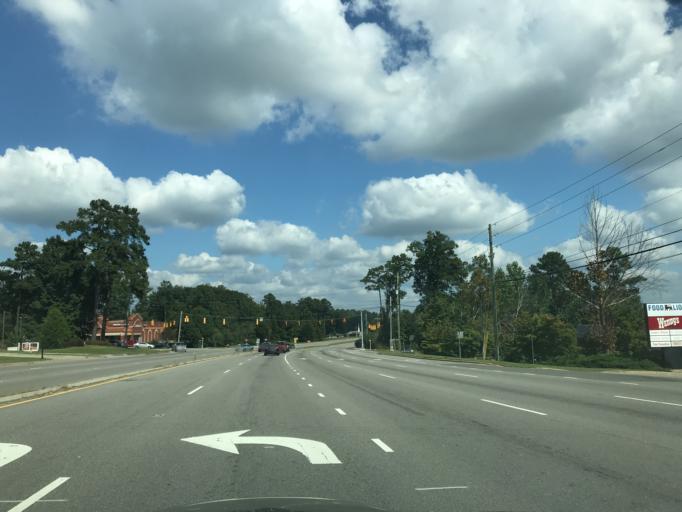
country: US
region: North Carolina
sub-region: Wake County
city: Rolesville
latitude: 35.8750
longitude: -78.5413
